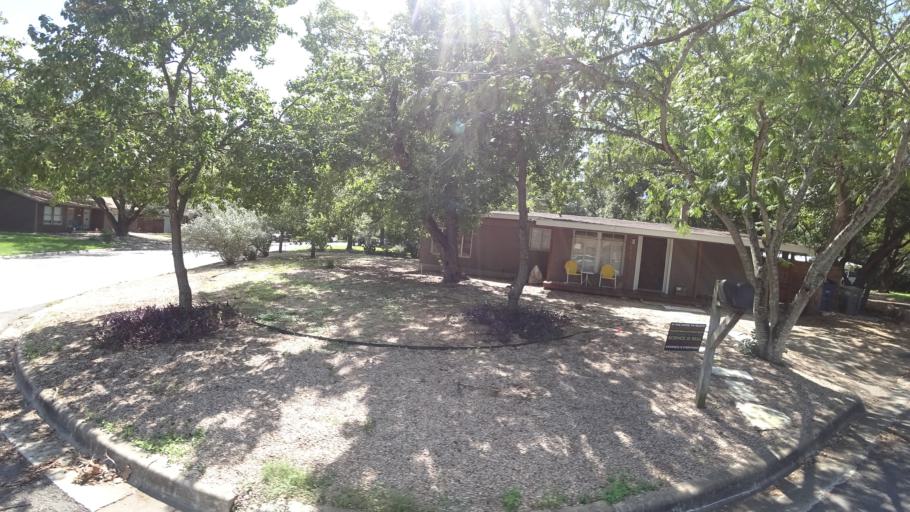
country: US
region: Texas
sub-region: Travis County
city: Austin
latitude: 30.3152
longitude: -97.6880
